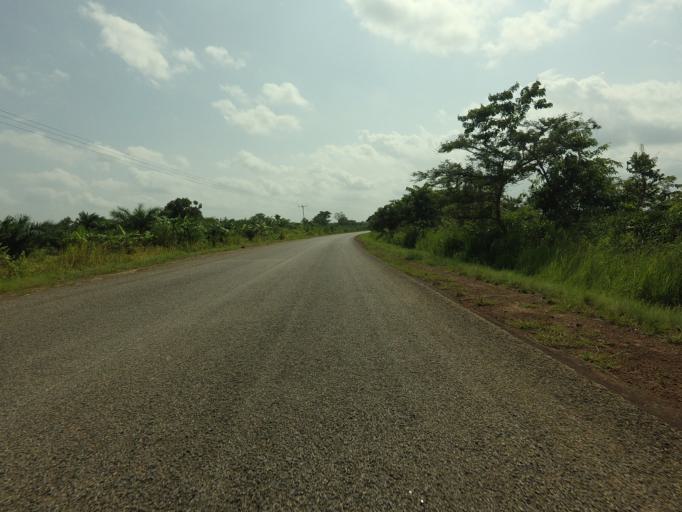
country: GH
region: Volta
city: Ho
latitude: 6.3930
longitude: 0.8126
